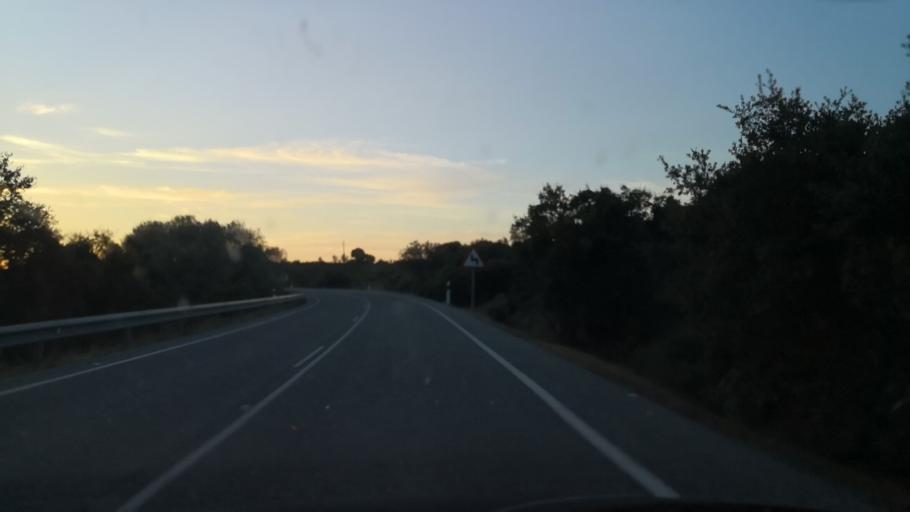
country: ES
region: Extremadura
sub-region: Provincia de Caceres
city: Alcantara
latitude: 39.6863
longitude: -6.8630
